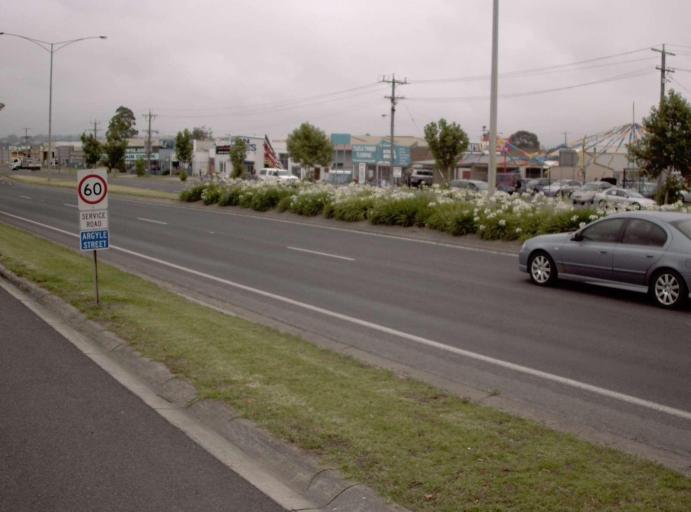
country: AU
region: Victoria
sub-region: Latrobe
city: Traralgon
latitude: -38.1911
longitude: 146.5600
